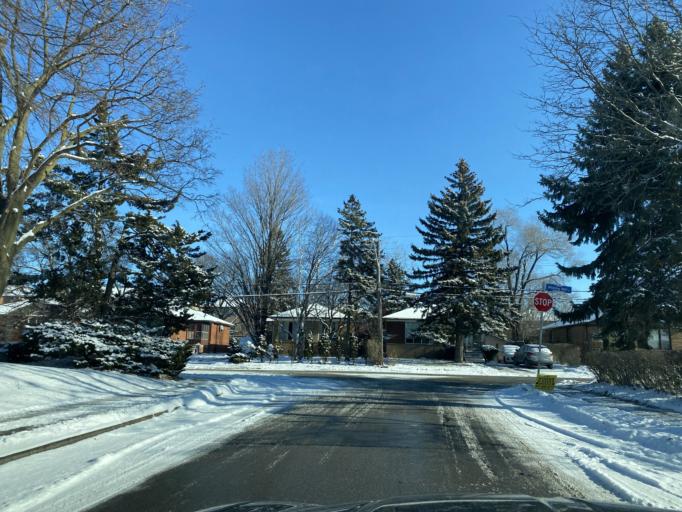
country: CA
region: Ontario
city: Scarborough
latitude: 43.7705
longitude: -79.3112
